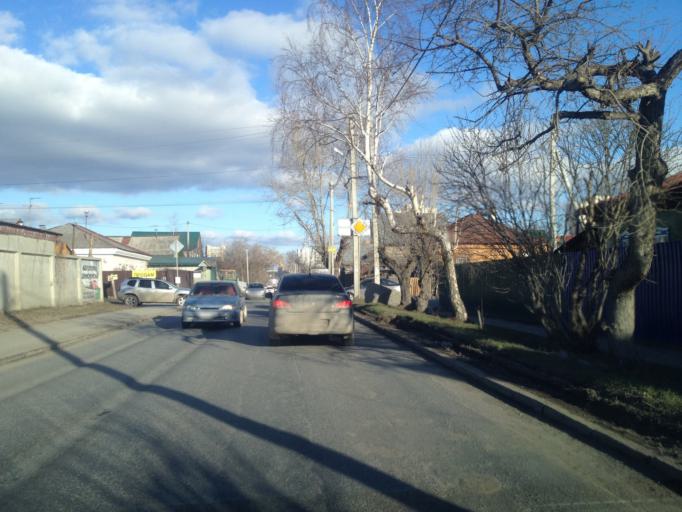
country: RU
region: Sverdlovsk
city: Sovkhoznyy
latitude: 56.8076
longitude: 60.5702
